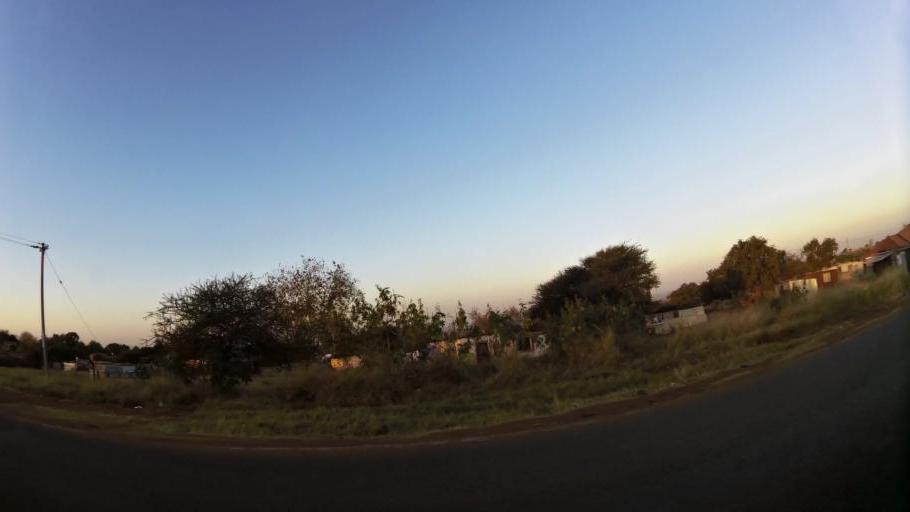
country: ZA
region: North-West
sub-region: Bojanala Platinum District Municipality
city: Rustenburg
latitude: -25.6275
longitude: 27.1986
